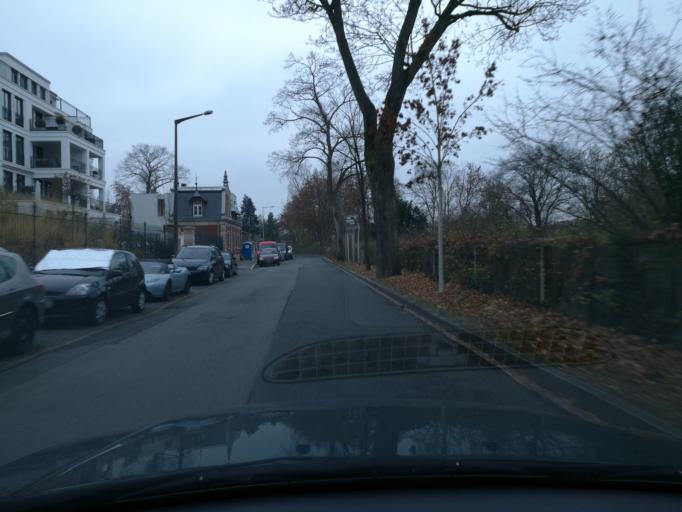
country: DE
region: Bavaria
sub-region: Regierungsbezirk Mittelfranken
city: Furth
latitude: 49.4667
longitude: 10.9833
